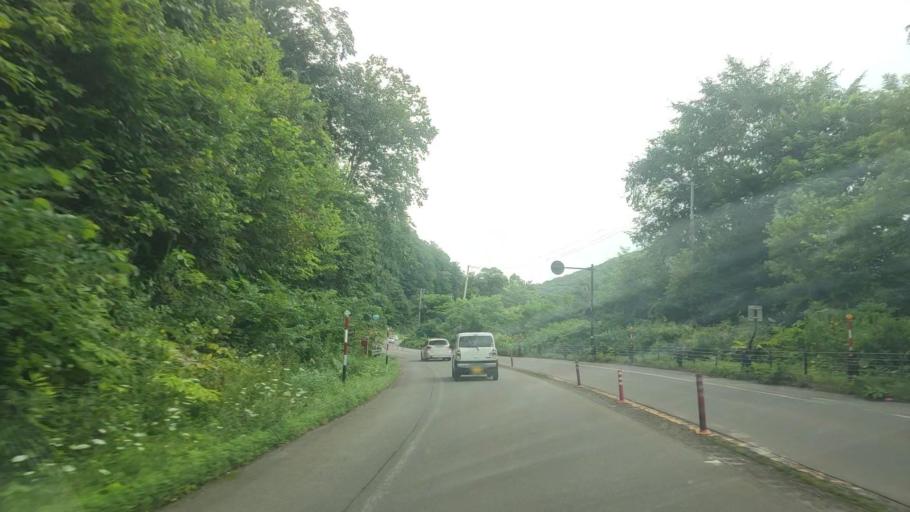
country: JP
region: Hokkaido
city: Nanae
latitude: 41.9724
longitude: 140.6495
